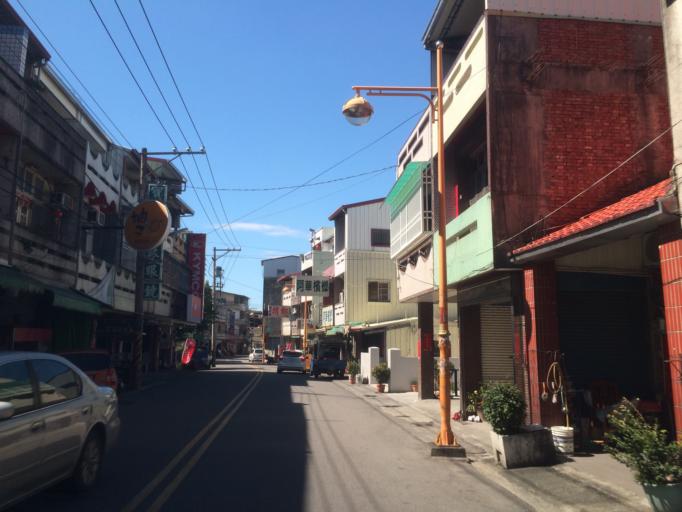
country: TW
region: Taiwan
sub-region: Yunlin
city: Douliu
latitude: 23.7025
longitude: 120.6002
